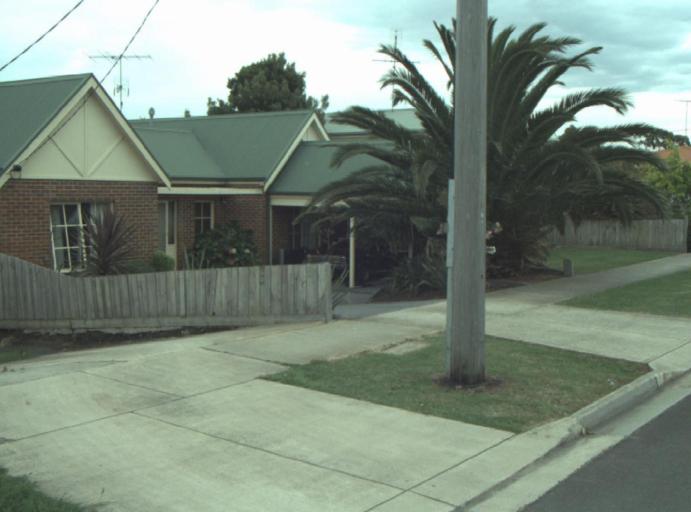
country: AU
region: Victoria
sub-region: Greater Geelong
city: Leopold
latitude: -38.1944
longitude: 144.4620
